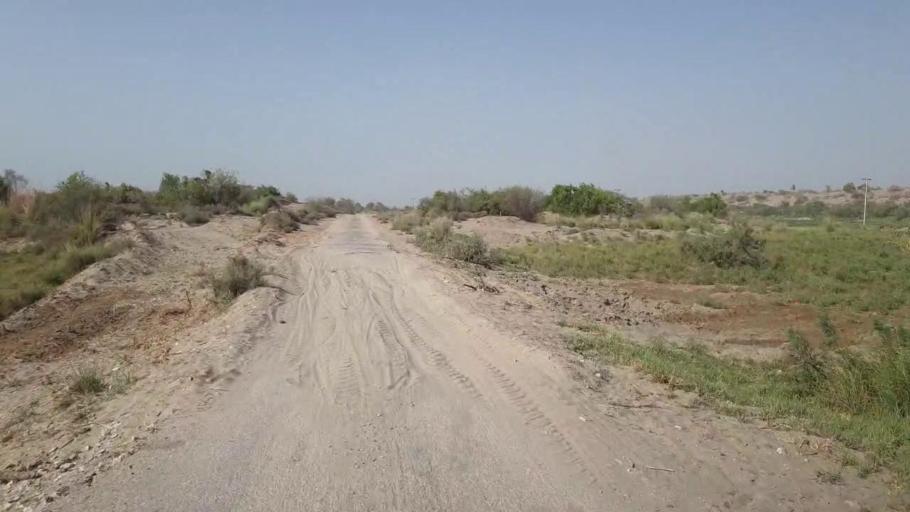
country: PK
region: Sindh
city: Jam Sahib
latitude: 26.6022
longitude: 68.9264
